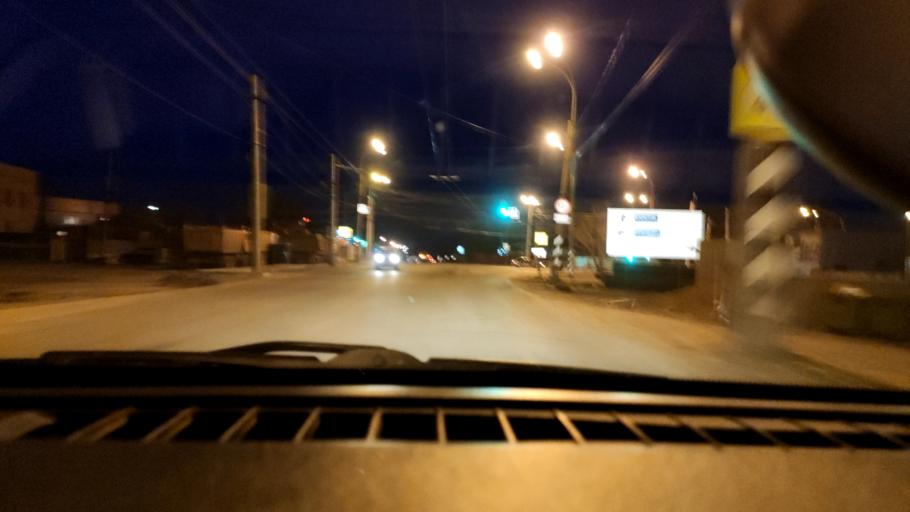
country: RU
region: Samara
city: Samara
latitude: 53.1369
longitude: 50.1034
